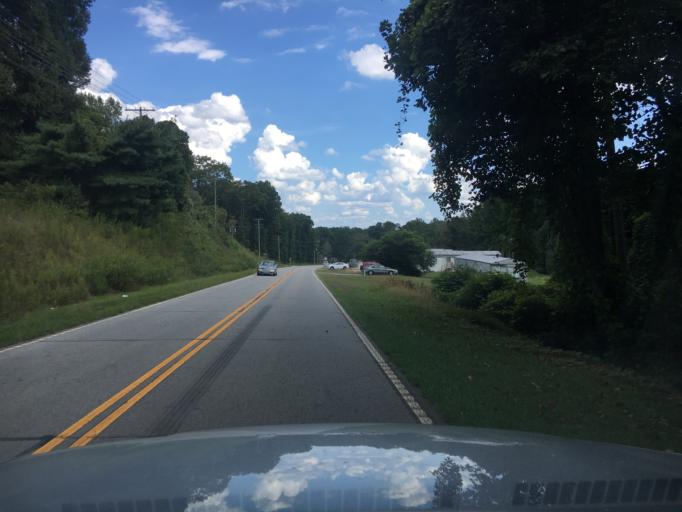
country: US
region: South Carolina
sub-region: Oconee County
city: Utica
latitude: 34.7111
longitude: -82.8897
